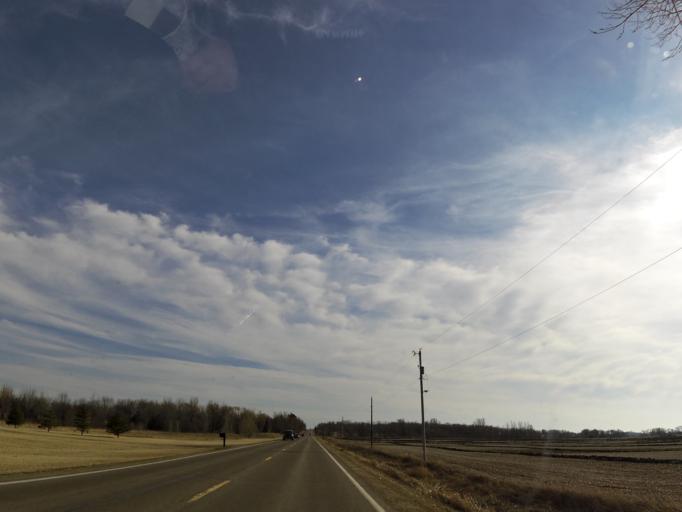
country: US
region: Minnesota
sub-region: Rice County
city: Northfield
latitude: 44.4972
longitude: -93.2000
